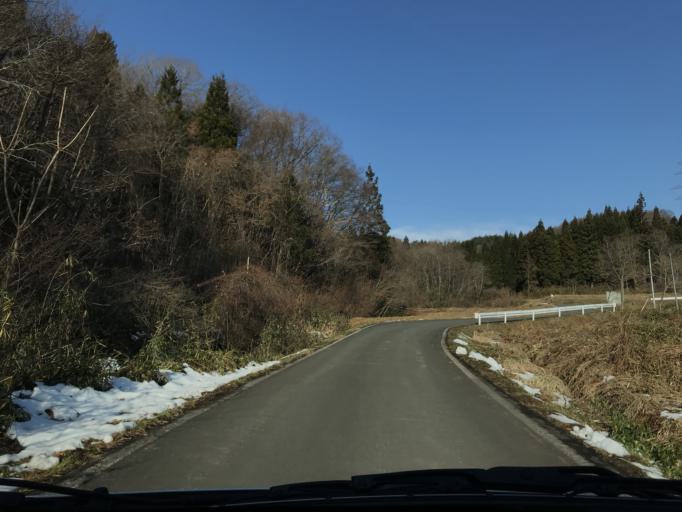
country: JP
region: Iwate
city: Ichinoseki
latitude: 38.9721
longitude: 141.0388
